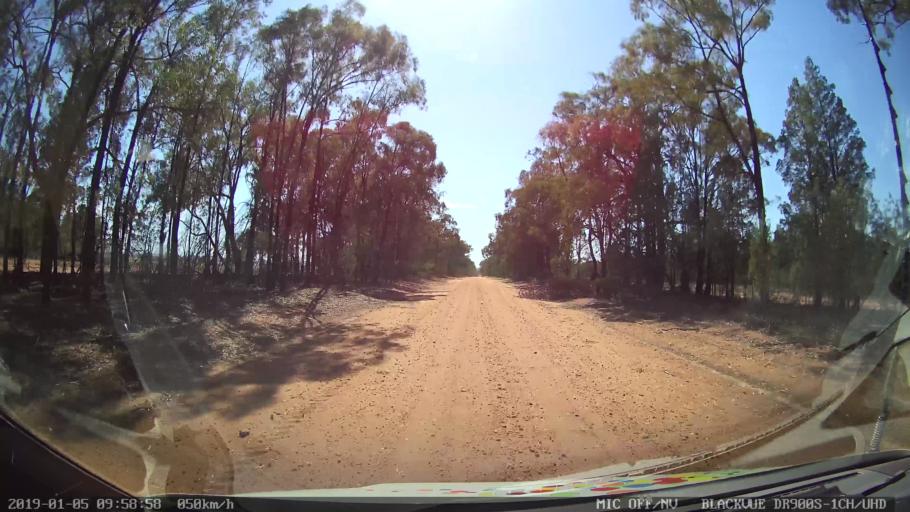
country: AU
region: New South Wales
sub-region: Gilgandra
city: Gilgandra
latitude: -31.6671
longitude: 148.8141
